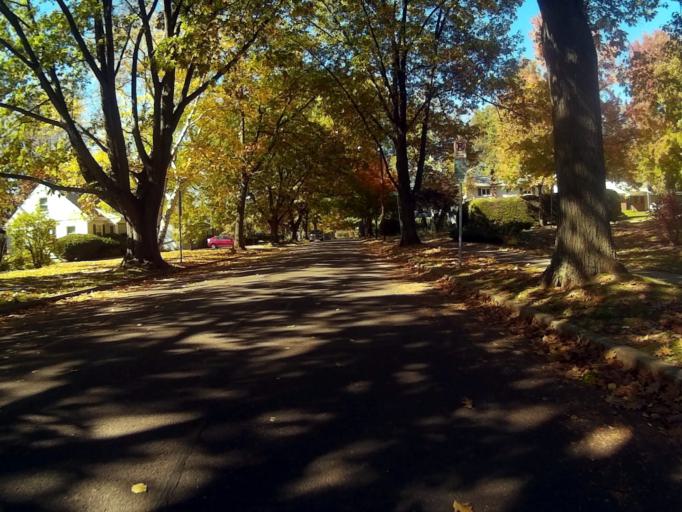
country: US
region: Pennsylvania
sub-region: Centre County
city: State College
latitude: 40.7932
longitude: -77.8781
